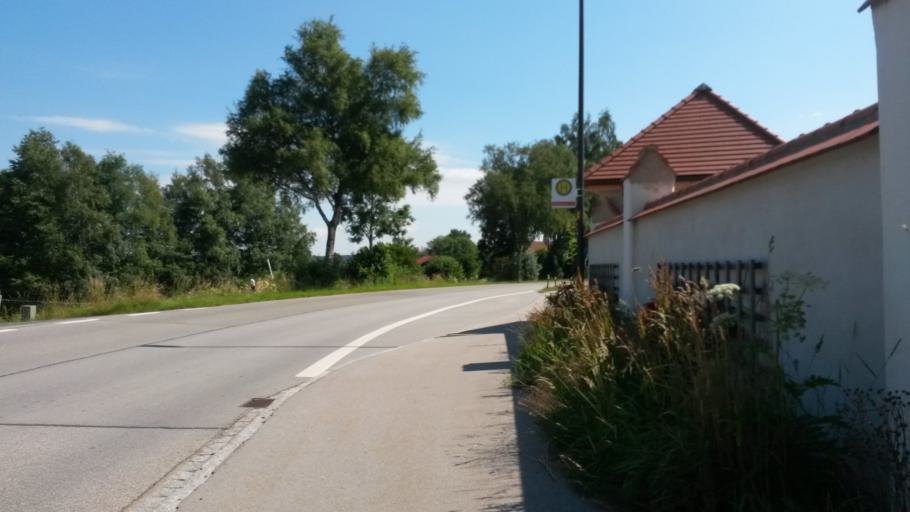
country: DE
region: Bavaria
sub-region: Upper Bavaria
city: Grabenstatt
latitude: 47.8332
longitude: 12.5289
